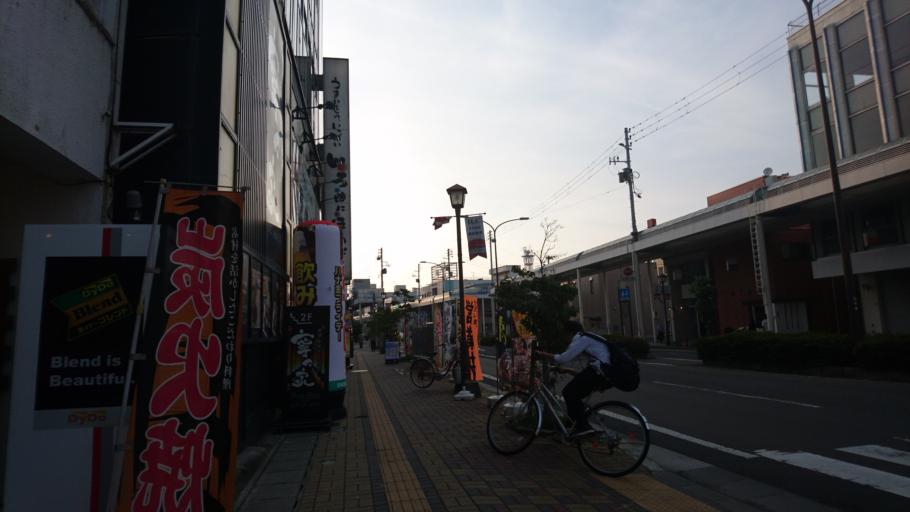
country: JP
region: Iwate
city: Mizusawa
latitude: 39.1390
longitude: 141.1454
